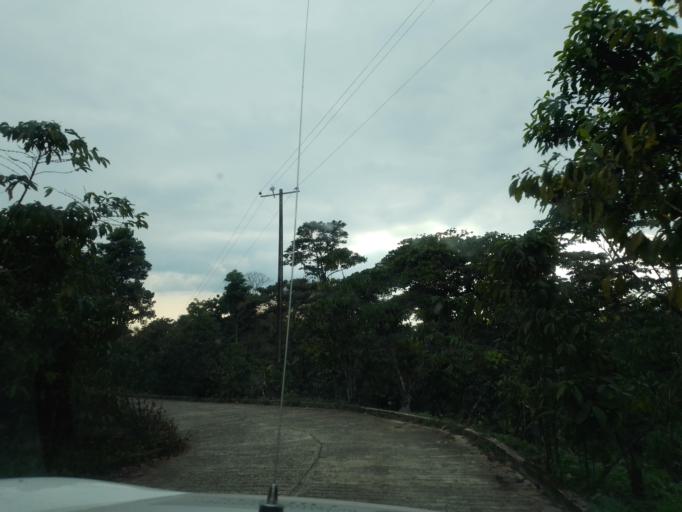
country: MX
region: Chiapas
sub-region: Union Juarez
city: Santo Domingo
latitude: 15.0498
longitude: -92.1183
